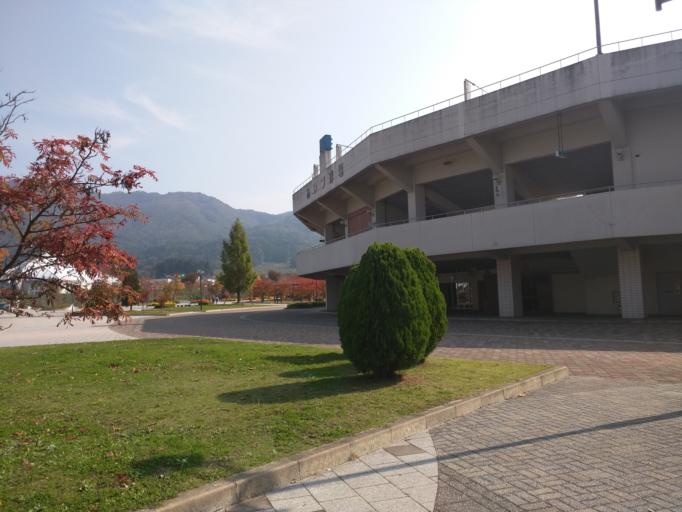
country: JP
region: Fukushima
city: Kitakata
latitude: 37.4615
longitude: 139.9256
